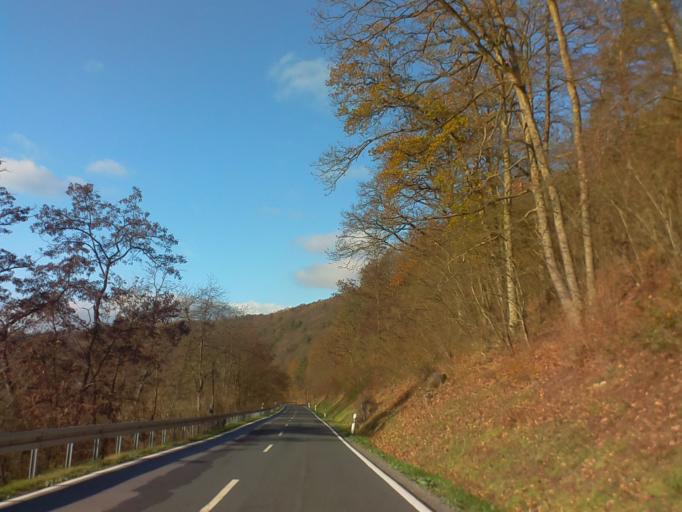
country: DE
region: Bavaria
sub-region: Regierungsbezirk Unterfranken
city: Niederlauer
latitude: 50.2975
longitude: 10.1469
